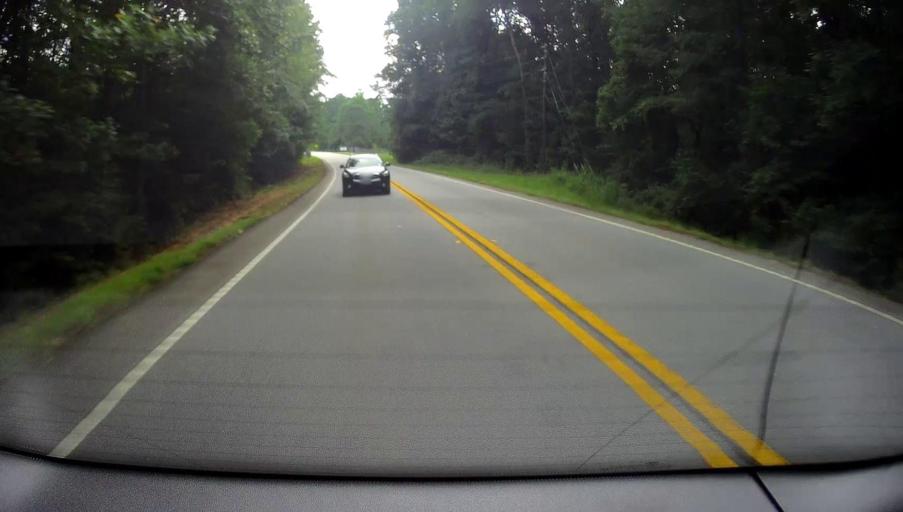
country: US
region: Georgia
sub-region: Coweta County
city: Senoia
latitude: 33.1566
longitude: -84.5849
